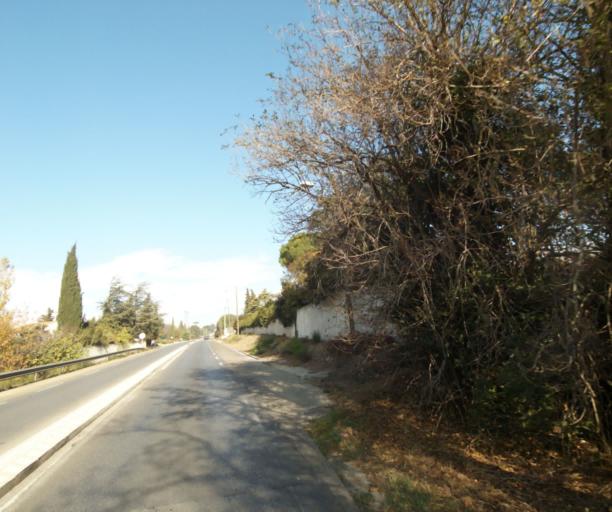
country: FR
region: Provence-Alpes-Cote d'Azur
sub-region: Departement des Bouches-du-Rhone
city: Allauch
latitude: 43.3185
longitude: 5.4948
